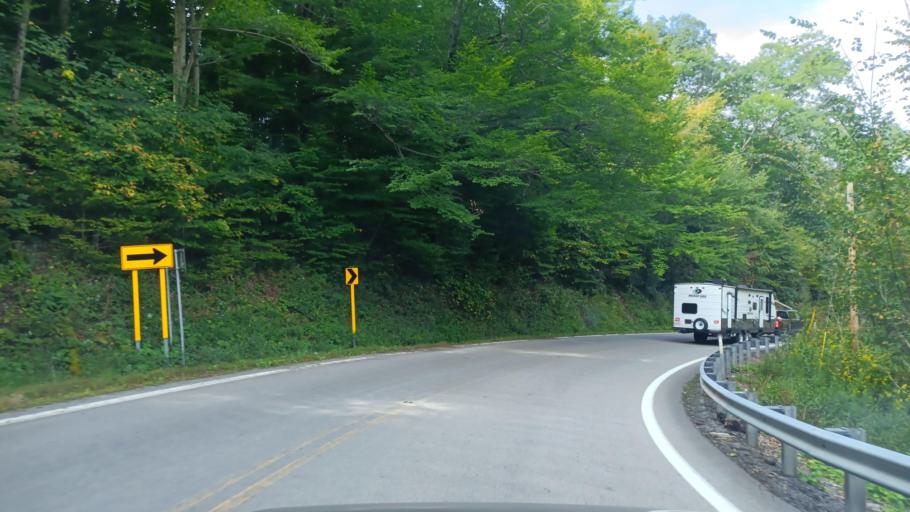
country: US
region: West Virginia
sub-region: Preston County
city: Terra Alta
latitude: 39.3004
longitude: -79.6123
